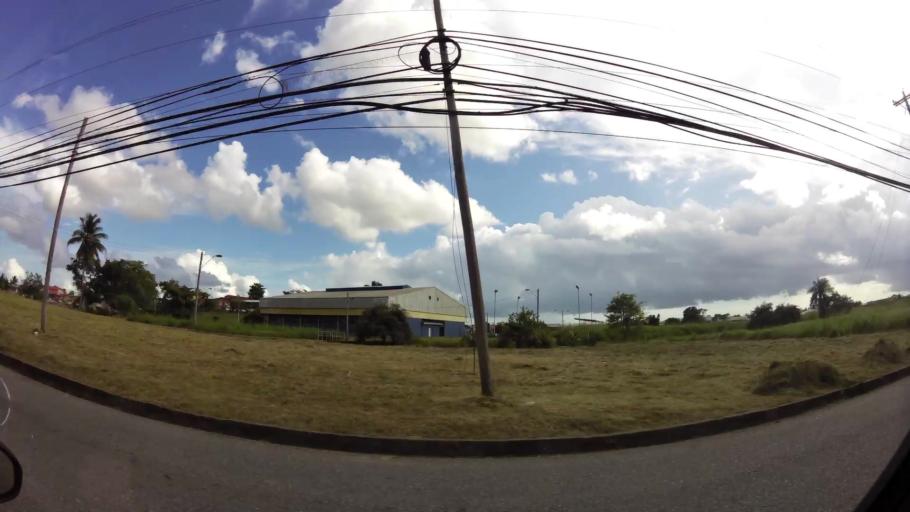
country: TT
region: City of San Fernando
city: Mon Repos
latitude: 10.2673
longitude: -61.4512
